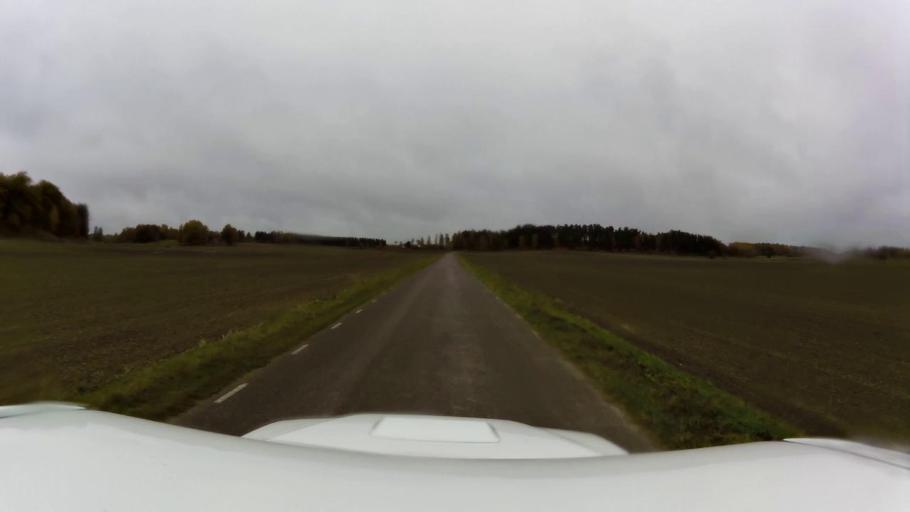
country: SE
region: OEstergoetland
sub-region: Norrkopings Kommun
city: Kimstad
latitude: 58.3938
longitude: 15.9496
